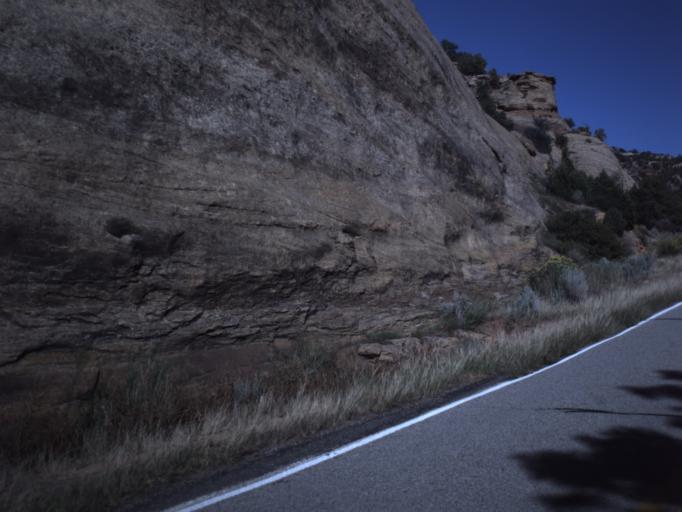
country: US
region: Utah
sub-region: San Juan County
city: Monticello
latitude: 37.9855
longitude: -109.5152
